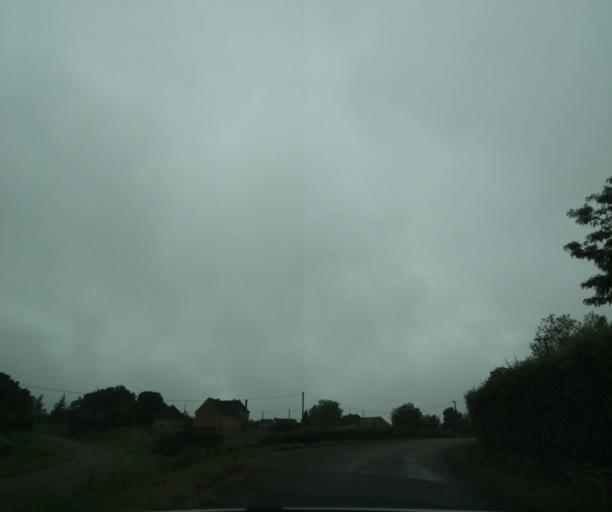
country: FR
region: Bourgogne
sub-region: Departement de Saone-et-Loire
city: Charolles
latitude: 46.4006
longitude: 4.1948
